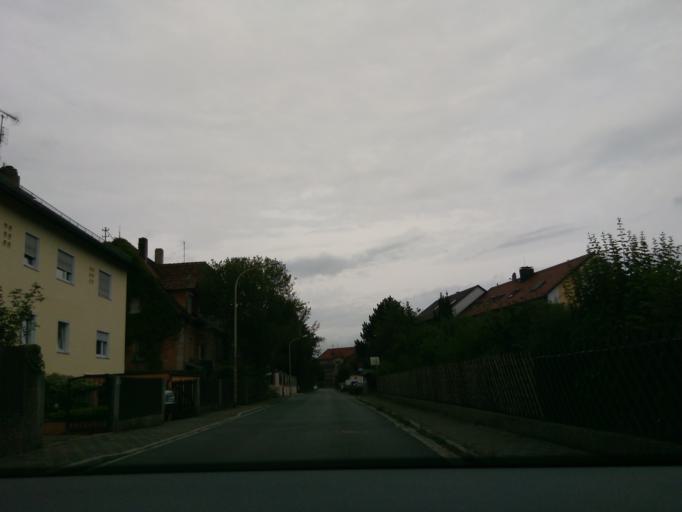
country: DE
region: Bavaria
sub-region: Regierungsbezirk Mittelfranken
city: Cadolzburg
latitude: 49.4593
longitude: 10.8604
